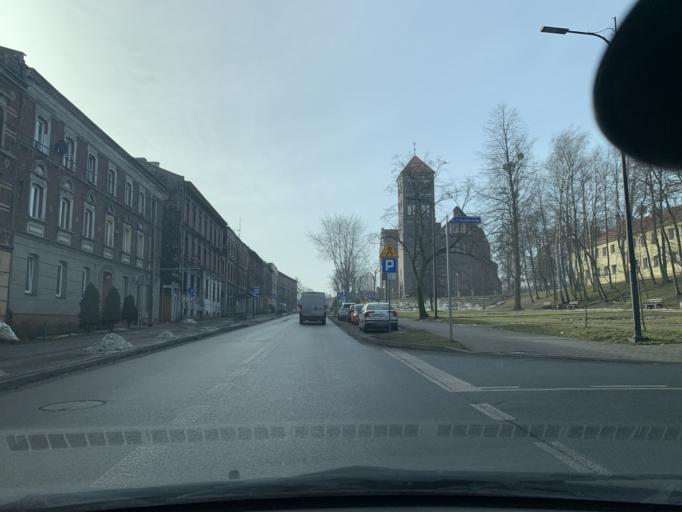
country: PL
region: Silesian Voivodeship
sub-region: Ruda Slaska
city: Ruda Slaska
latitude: 50.3211
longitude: 18.8571
